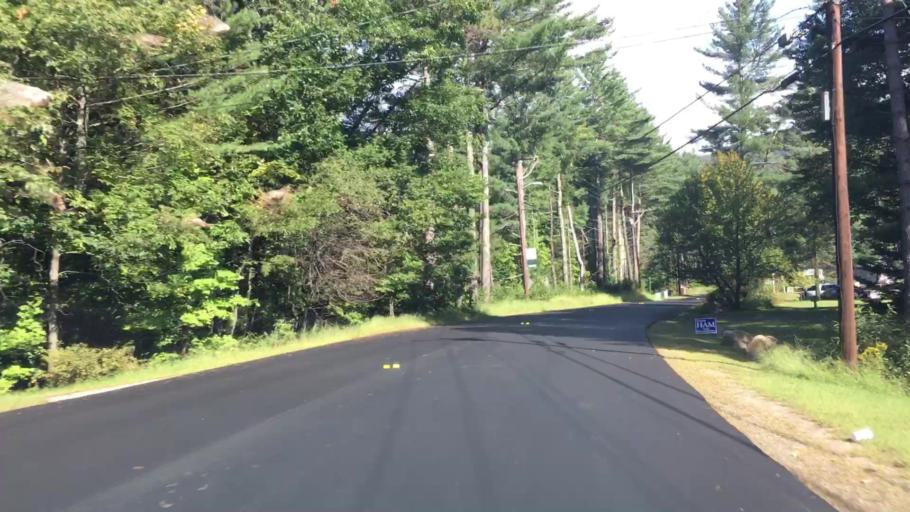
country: US
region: New Hampshire
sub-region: Grafton County
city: Woodstock
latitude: 44.0327
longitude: -71.6980
